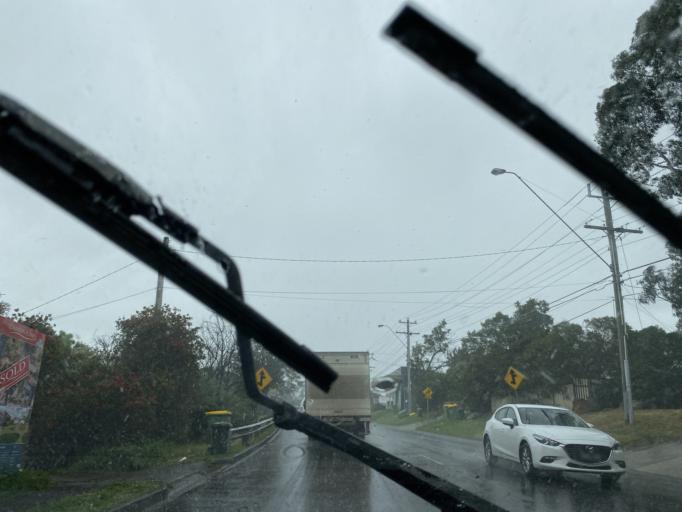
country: AU
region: Victoria
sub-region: Banyule
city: Montmorency
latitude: -37.7150
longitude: 145.1153
